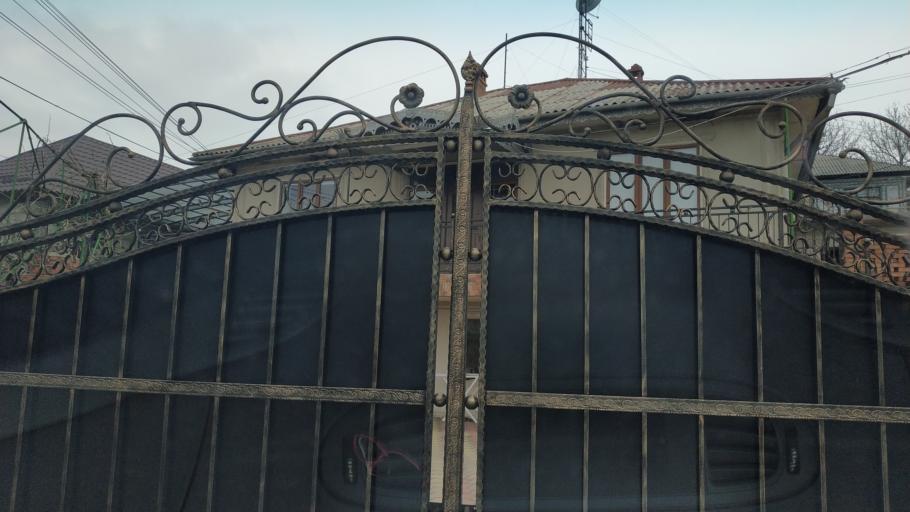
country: MD
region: Chisinau
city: Singera
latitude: 46.9198
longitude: 28.9832
